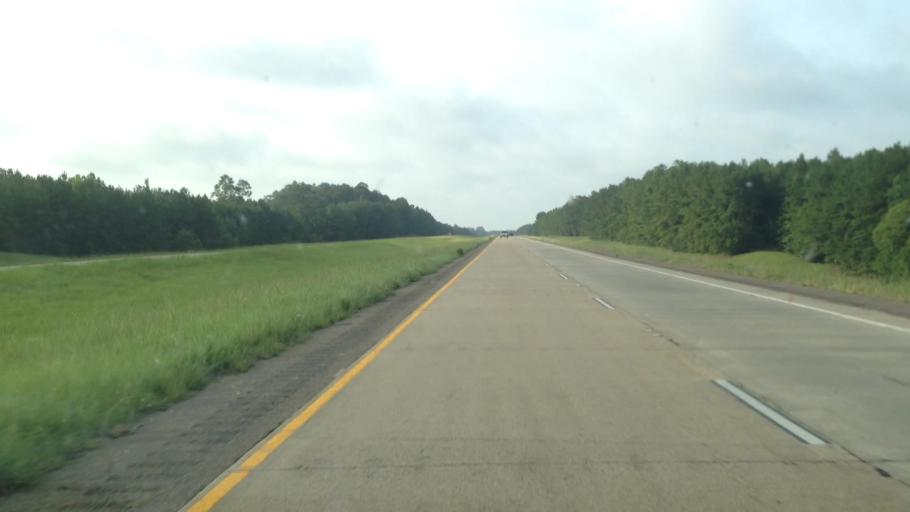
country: US
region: Louisiana
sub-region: Rapides Parish
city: Lecompte
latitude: 31.0547
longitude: -92.4242
